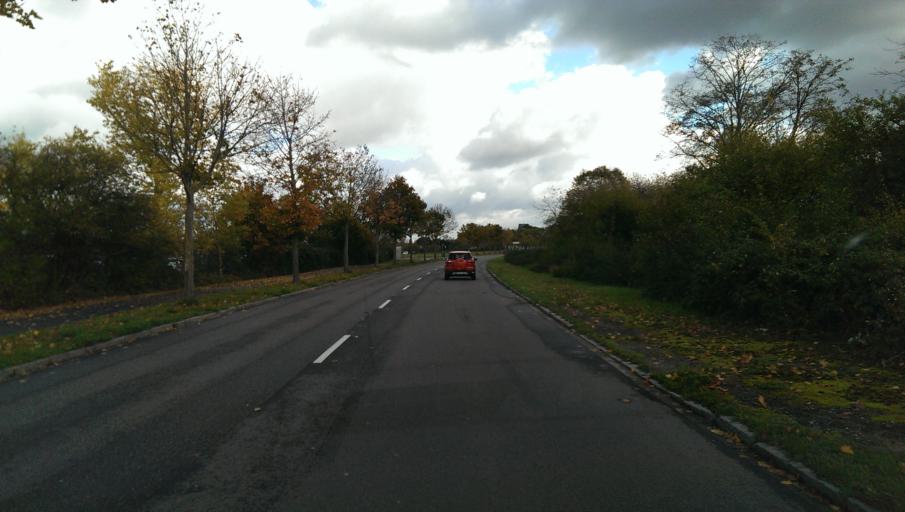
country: DE
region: Baden-Wuerttemberg
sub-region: Karlsruhe Region
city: Karlsruhe
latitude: 49.0379
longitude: 8.3565
